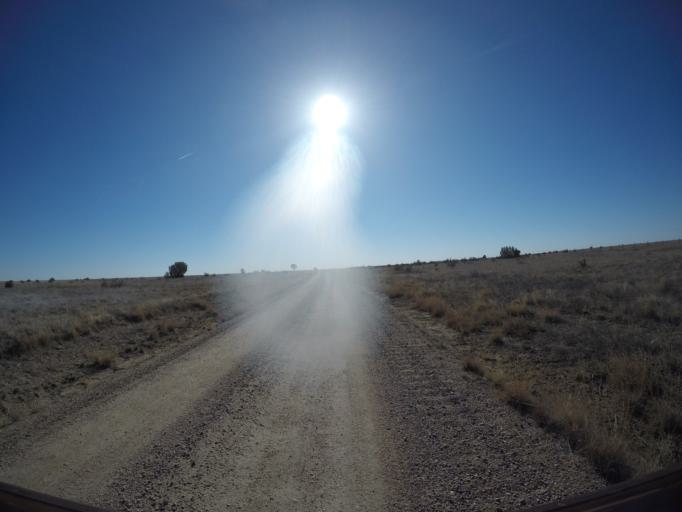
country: US
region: Colorado
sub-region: Otero County
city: La Junta
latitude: 37.6578
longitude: -103.6056
